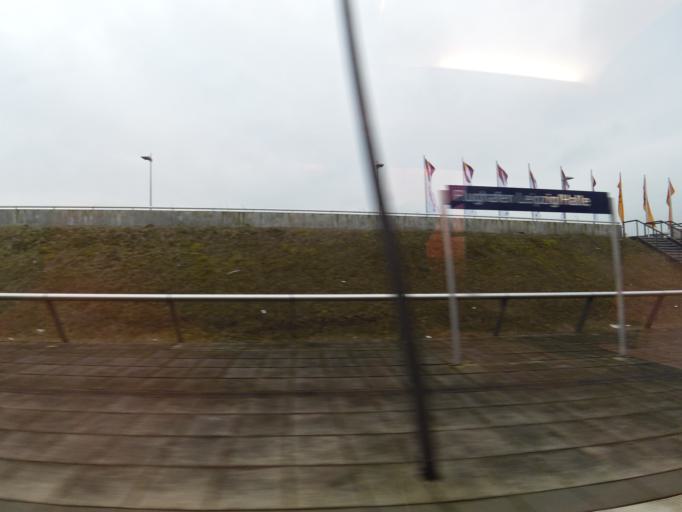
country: DE
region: Saxony
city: Schkeuditz
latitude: 51.4228
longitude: 12.2265
